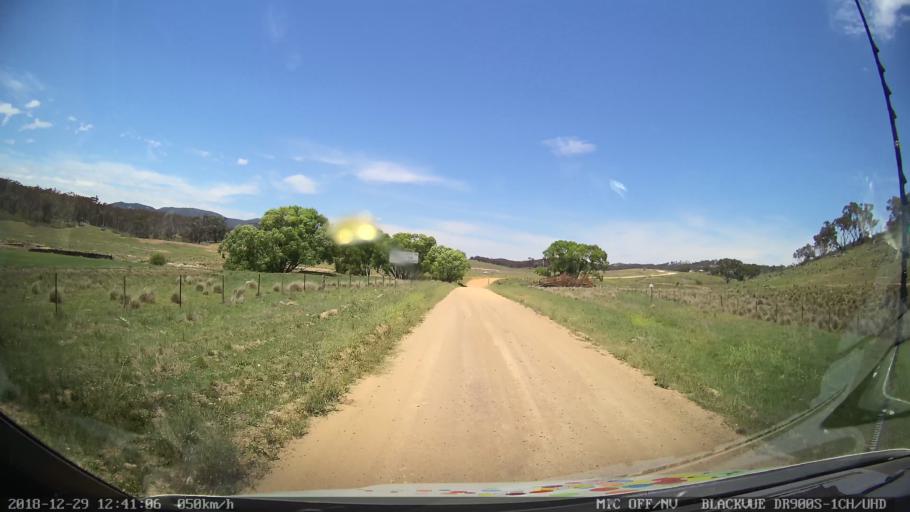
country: AU
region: Australian Capital Territory
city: Macarthur
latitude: -35.6065
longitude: 149.2230
